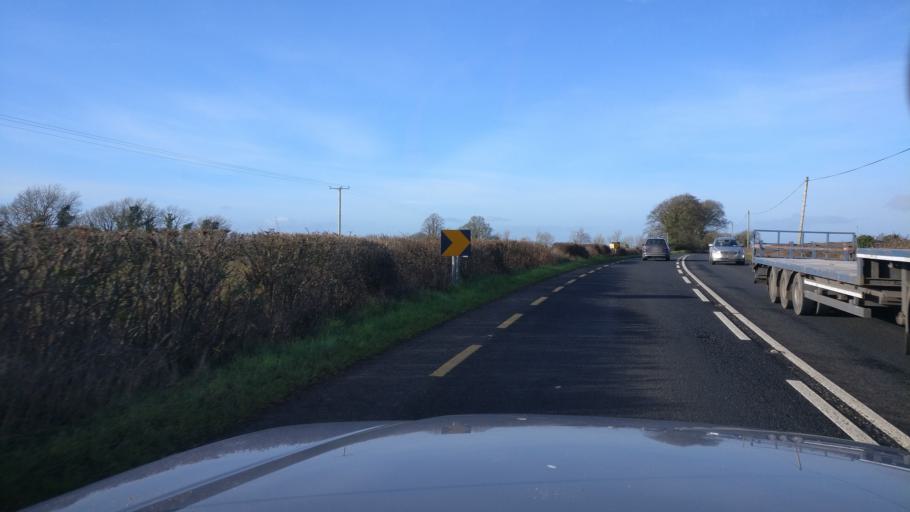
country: IE
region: Leinster
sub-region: Uibh Fhaili
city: Tullamore
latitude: 53.2007
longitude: -7.4315
